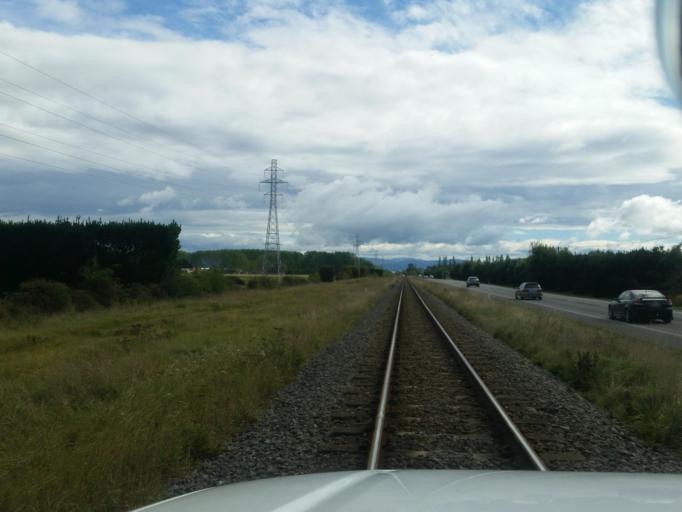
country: NZ
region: Canterbury
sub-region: Waimakariri District
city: Kaiapoi
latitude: -43.3394
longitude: 172.6118
